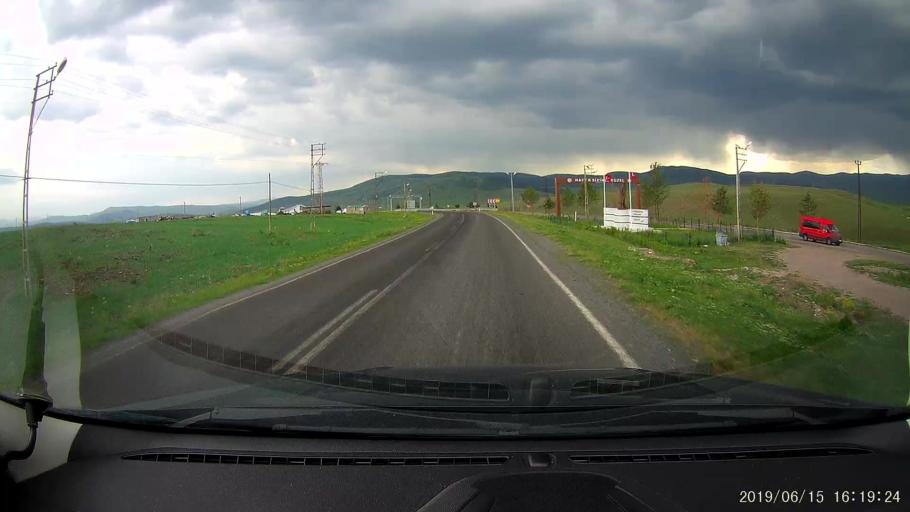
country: TR
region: Ardahan
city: Hanak
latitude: 41.2290
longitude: 42.8507
